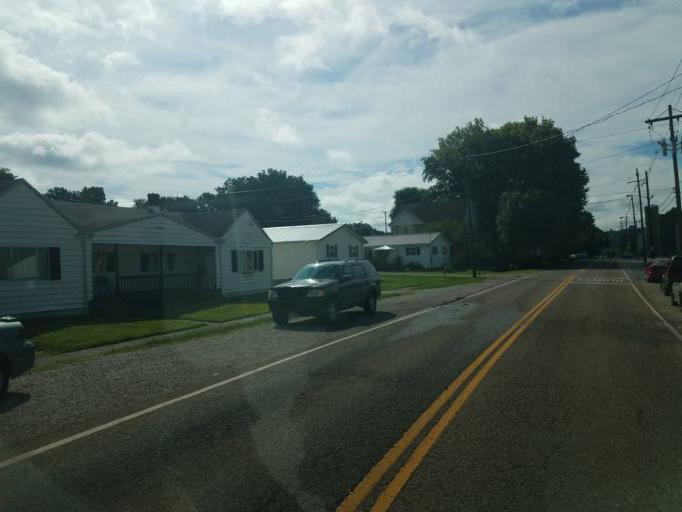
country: US
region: Ohio
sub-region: Gallia County
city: Gallipolis
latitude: 38.8108
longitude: -82.2084
